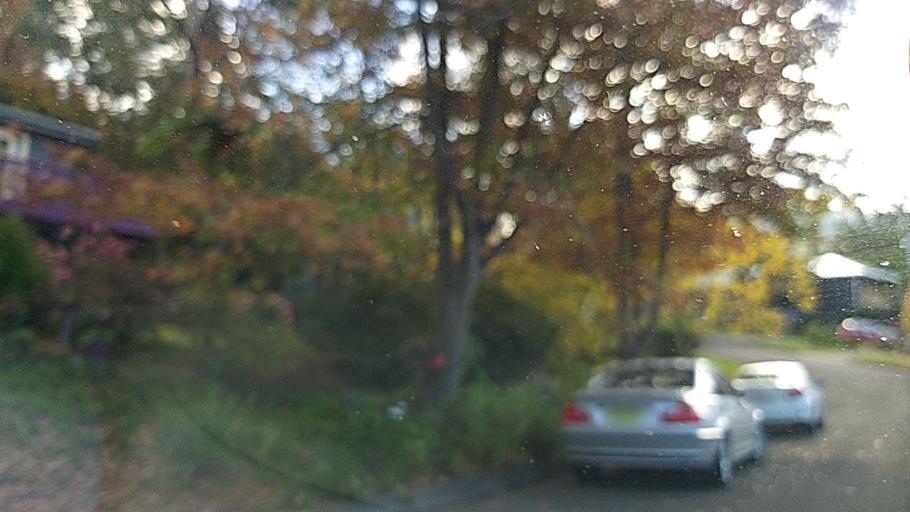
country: AU
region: New South Wales
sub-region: Wollongong
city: Cordeaux Heights
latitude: -34.4335
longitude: 150.8154
